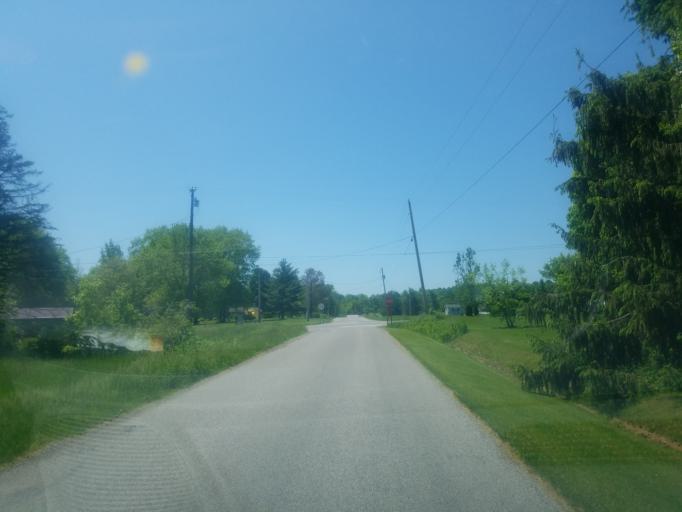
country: US
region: Ohio
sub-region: Huron County
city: Wakeman
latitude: 41.1829
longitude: -82.3722
